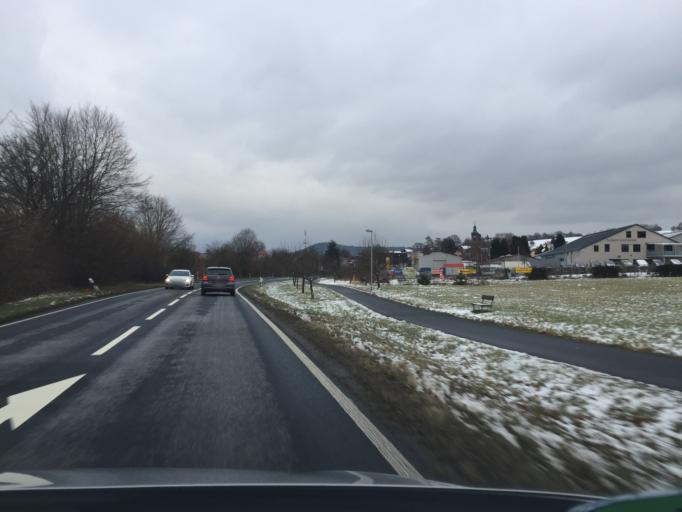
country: DE
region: Bavaria
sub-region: Regierungsbezirk Unterfranken
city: Blankenbach
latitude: 50.0608
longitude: 9.2281
